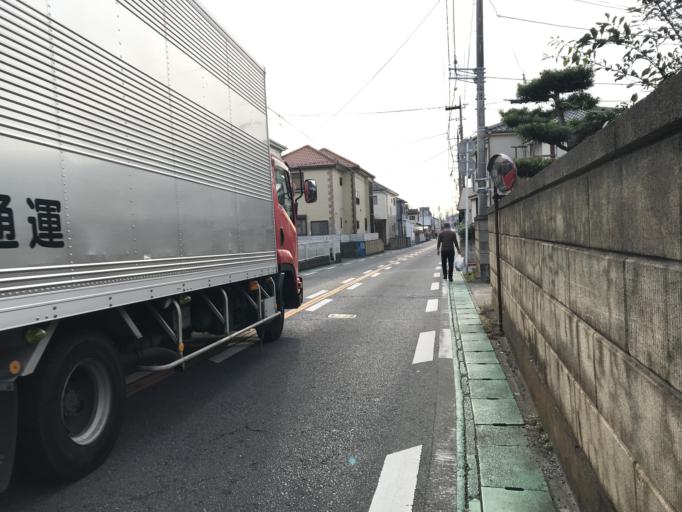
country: JP
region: Chiba
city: Shiroi
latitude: 35.7676
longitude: 140.0079
